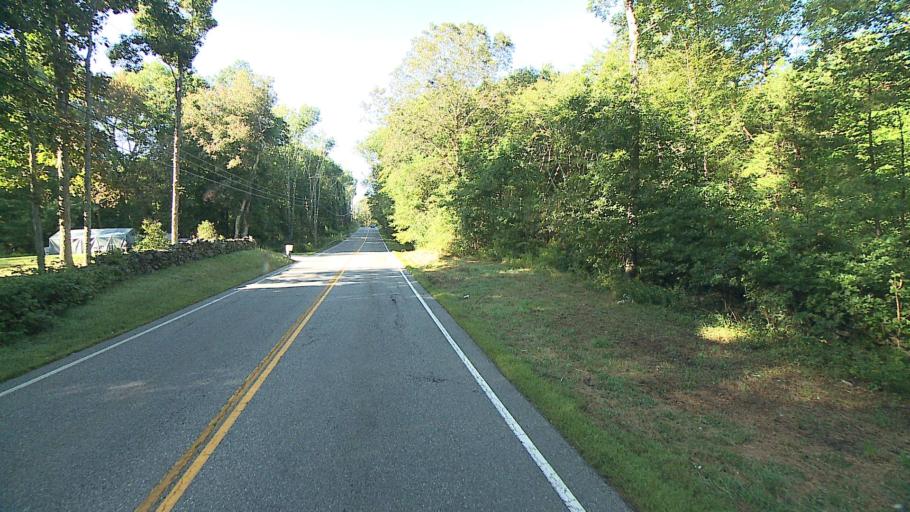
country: US
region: Connecticut
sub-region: New London County
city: Lisbon
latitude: 41.5777
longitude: -71.9997
